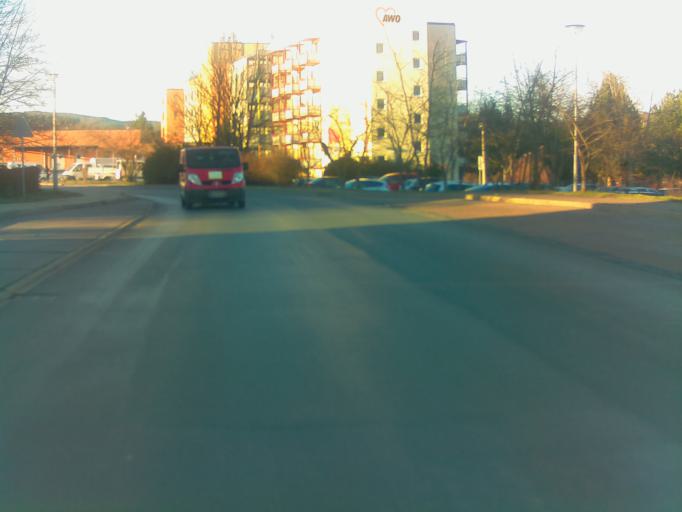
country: DE
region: Thuringia
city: Rudolstadt
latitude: 50.7010
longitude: 11.3212
